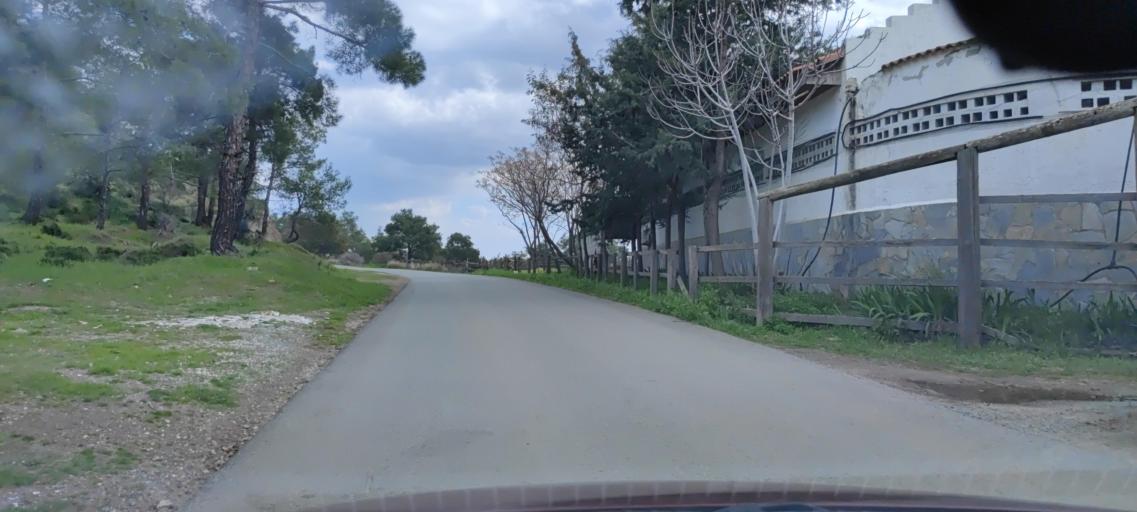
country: CY
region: Lefkosia
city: Lythrodontas
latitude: 34.9386
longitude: 33.3166
